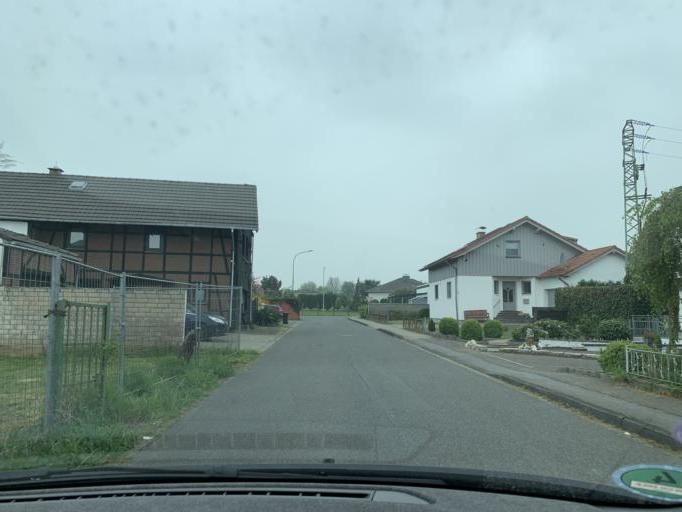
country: DE
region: North Rhine-Westphalia
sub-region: Regierungsbezirk Koln
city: Vettweiss
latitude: 50.6847
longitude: 6.5719
